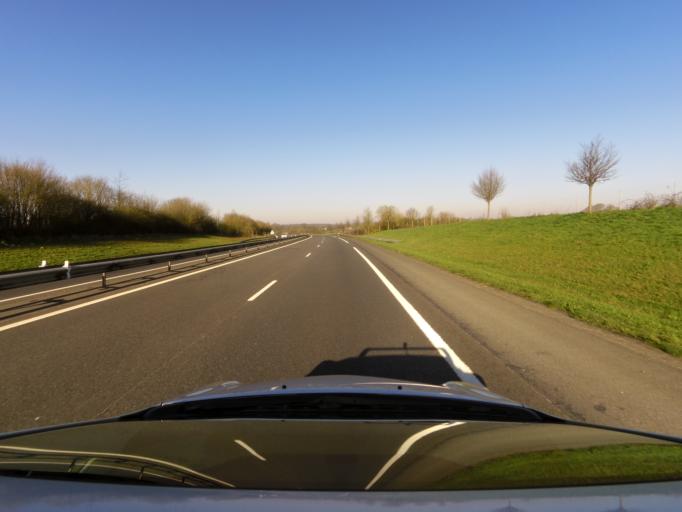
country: FR
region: Lower Normandy
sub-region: Departement du Calvados
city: Saint-Martin-des-Besaces
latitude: 49.0150
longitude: -0.8672
